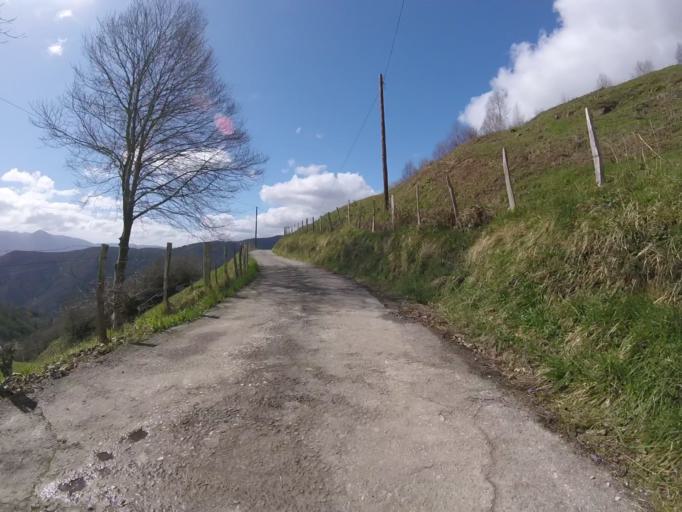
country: ES
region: Basque Country
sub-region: Provincia de Guipuzcoa
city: Albiztur
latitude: 43.1409
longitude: -2.1248
